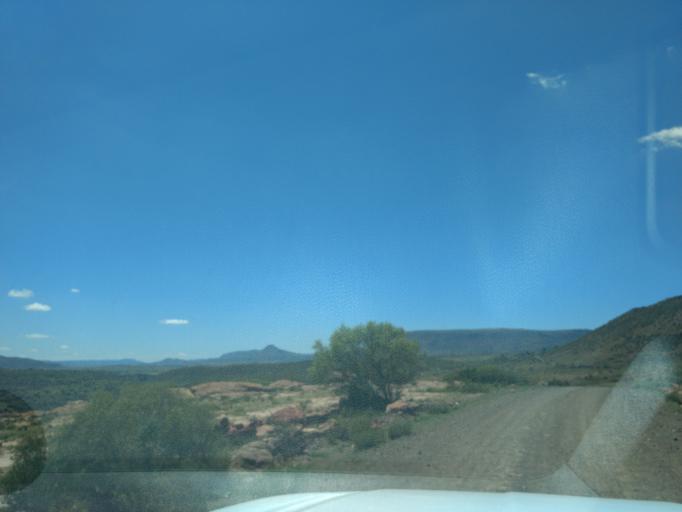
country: LS
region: Maseru
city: Maseru
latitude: -29.4532
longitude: 27.3687
